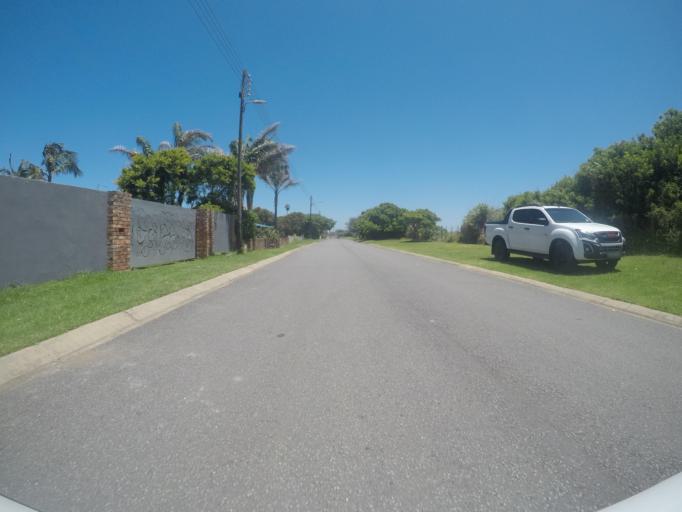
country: ZA
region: Eastern Cape
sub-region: Buffalo City Metropolitan Municipality
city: East London
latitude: -32.9506
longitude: 28.0111
